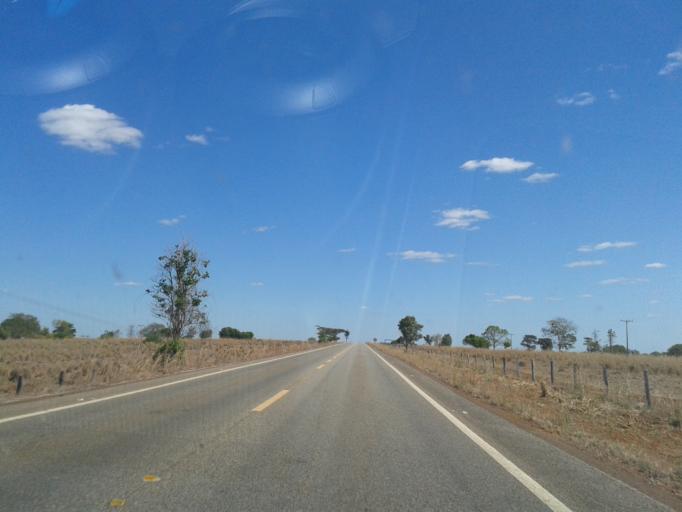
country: BR
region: Goias
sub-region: Sao Miguel Do Araguaia
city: Sao Miguel do Araguaia
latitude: -13.4122
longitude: -50.2670
